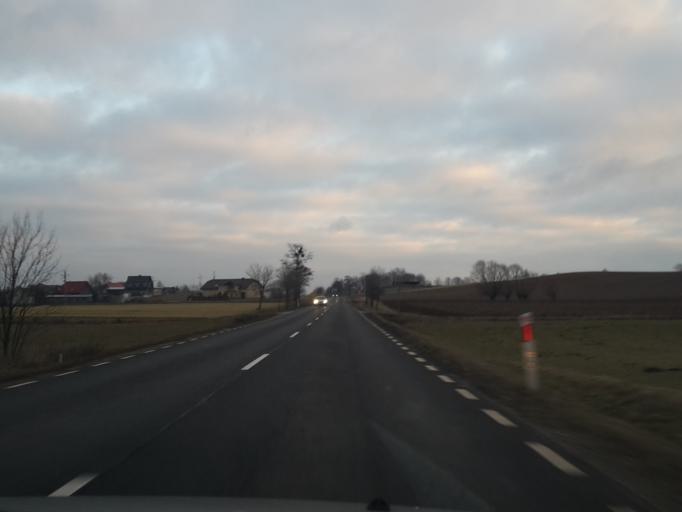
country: PL
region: Warmian-Masurian Voivodeship
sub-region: Powiat ilawski
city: Lubawa
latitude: 53.5598
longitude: 19.7737
